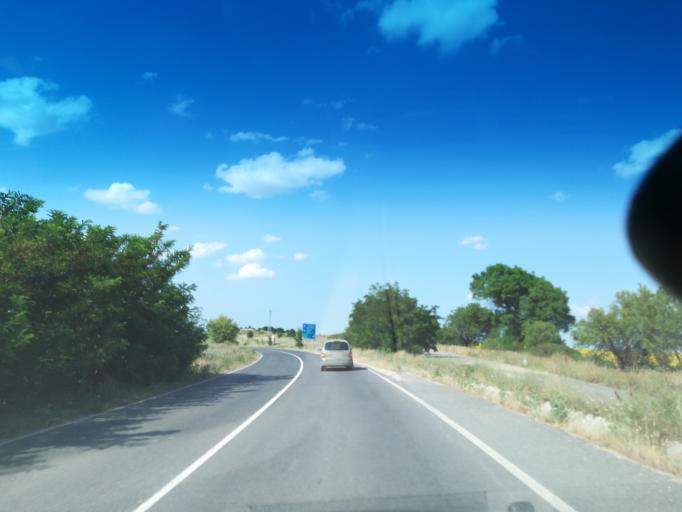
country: BG
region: Stara Zagora
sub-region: Obshtina Chirpan
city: Chirpan
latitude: 42.2468
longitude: 25.4114
